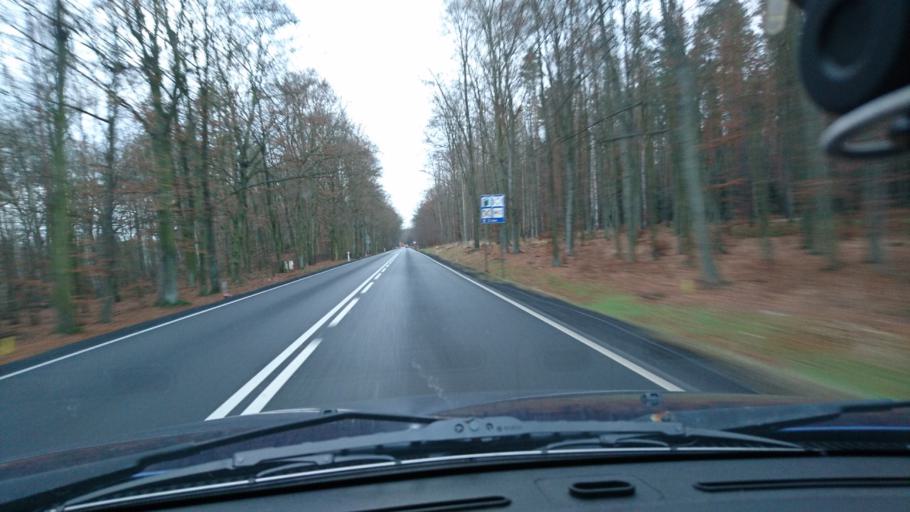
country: PL
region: Opole Voivodeship
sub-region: Powiat kluczborski
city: Kluczbork
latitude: 50.9620
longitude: 18.2872
